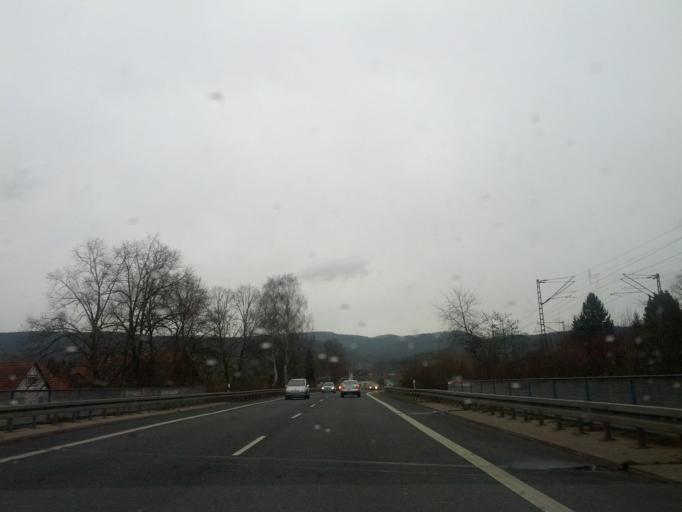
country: DE
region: Thuringia
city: Lindewerra
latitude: 51.2993
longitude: 9.9611
